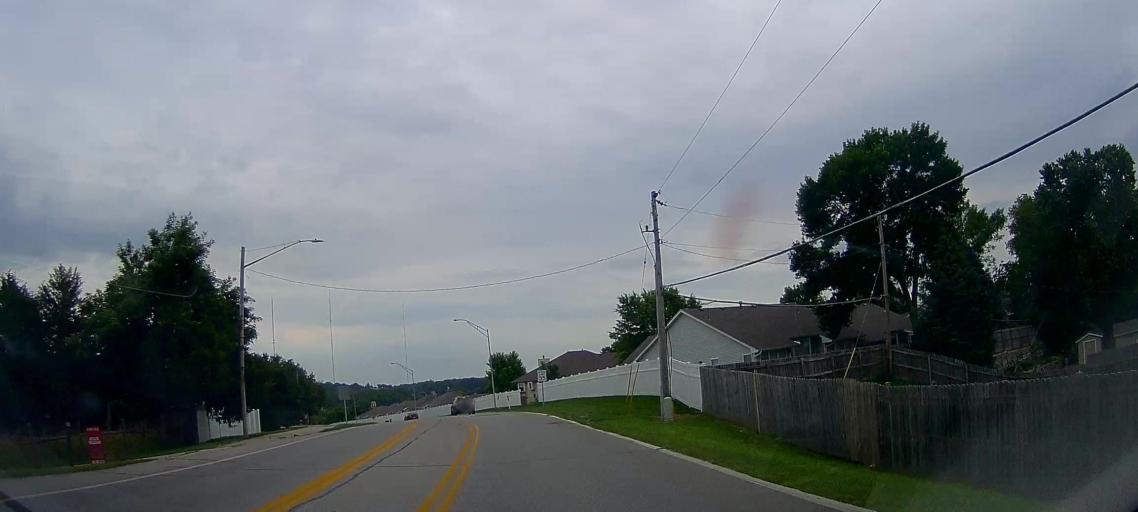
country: US
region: Nebraska
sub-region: Douglas County
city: Ralston
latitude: 41.3114
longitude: -96.0576
